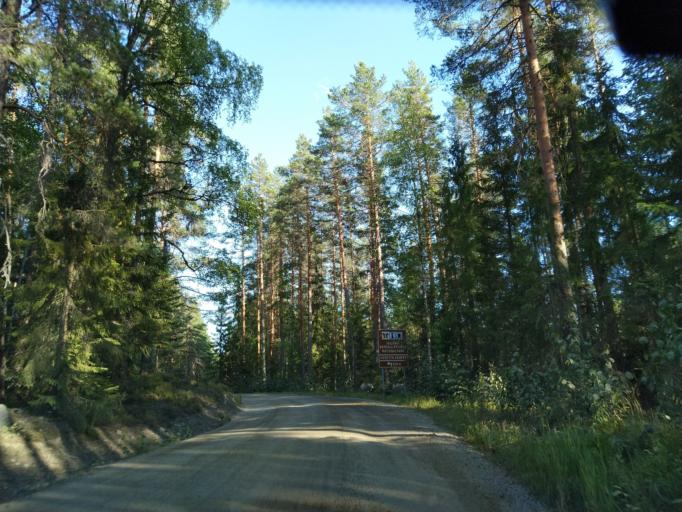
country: FI
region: Central Finland
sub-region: Jaemsae
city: Kuhmoinen
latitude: 61.6764
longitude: 24.9941
